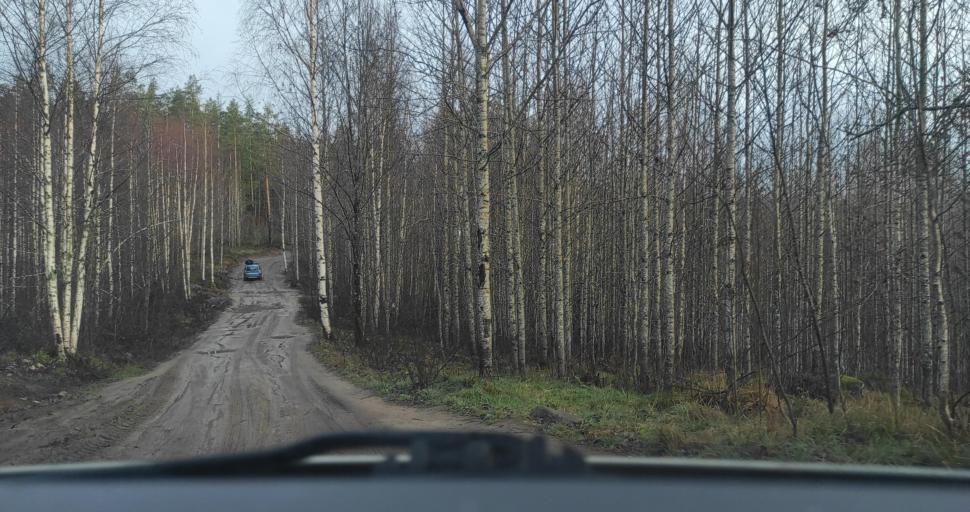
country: RU
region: Republic of Karelia
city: Pitkyaranta
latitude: 61.7412
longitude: 31.3918
